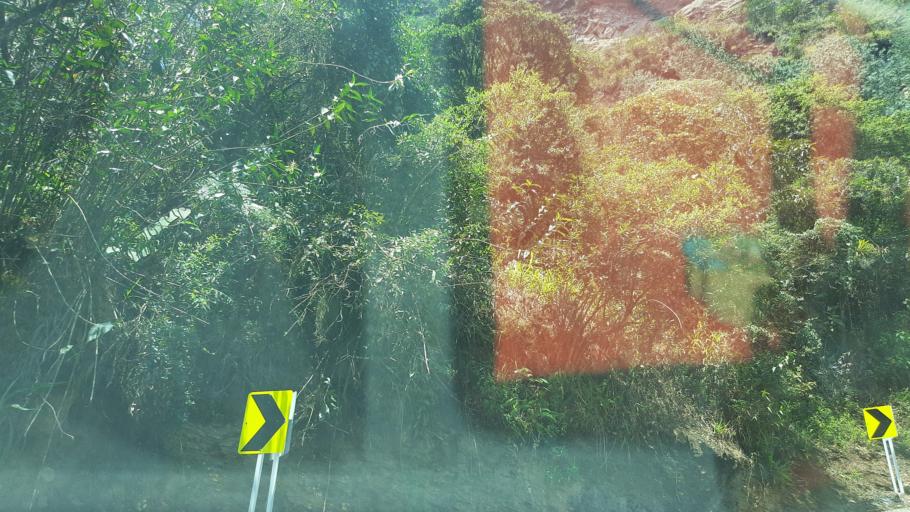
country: CO
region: Boyaca
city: Chinavita
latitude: 5.1309
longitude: -73.3894
